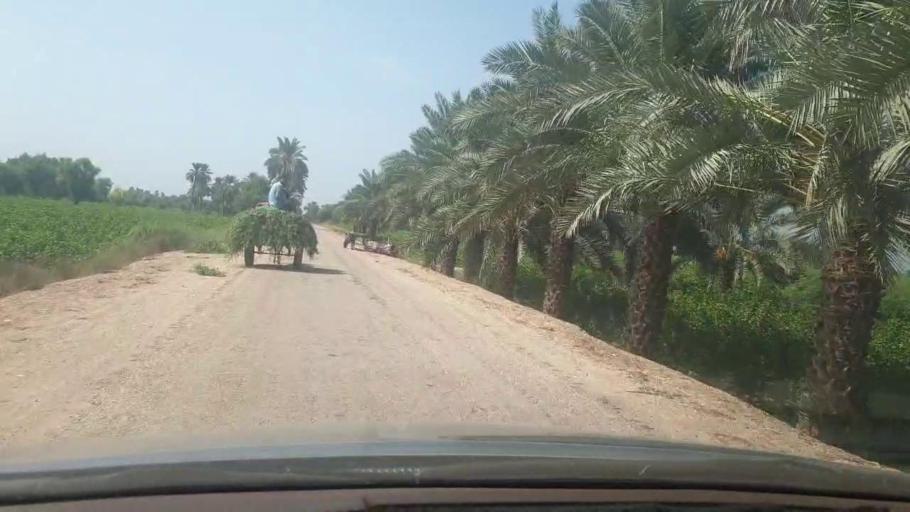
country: PK
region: Sindh
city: Ranipur
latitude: 27.2789
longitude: 68.5816
